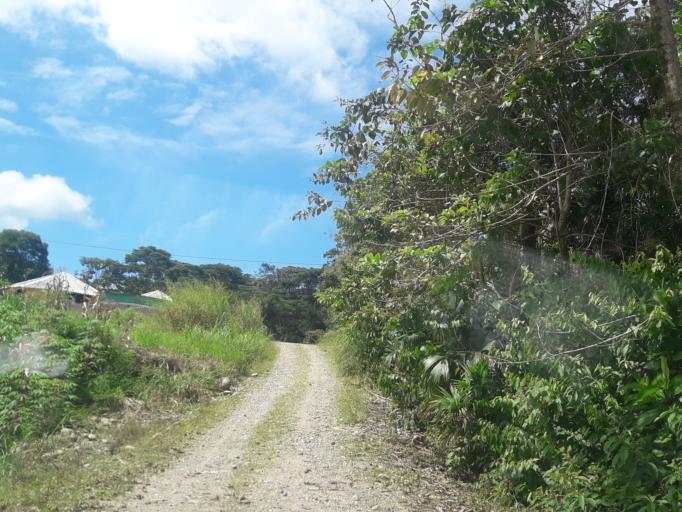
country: EC
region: Napo
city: Tena
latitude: -1.0177
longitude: -77.8629
